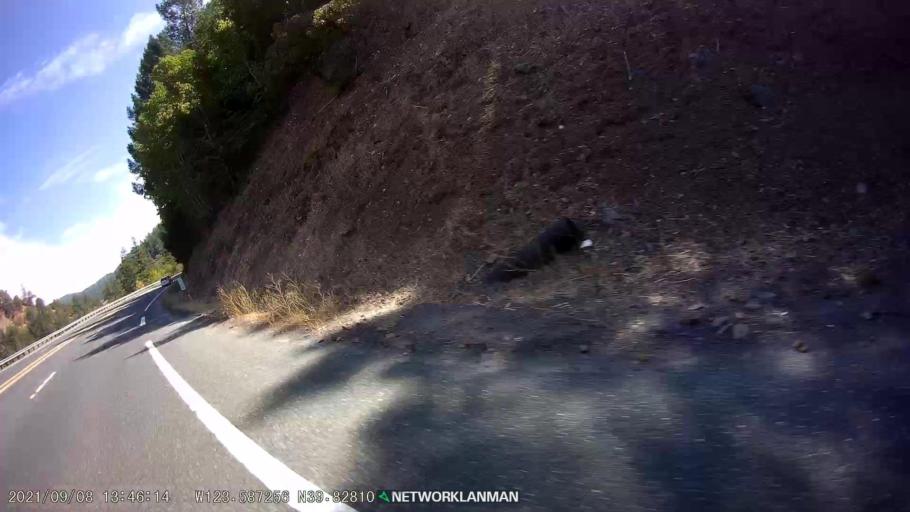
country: US
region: California
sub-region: Mendocino County
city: Laytonville
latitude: 39.8274
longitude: -123.5866
